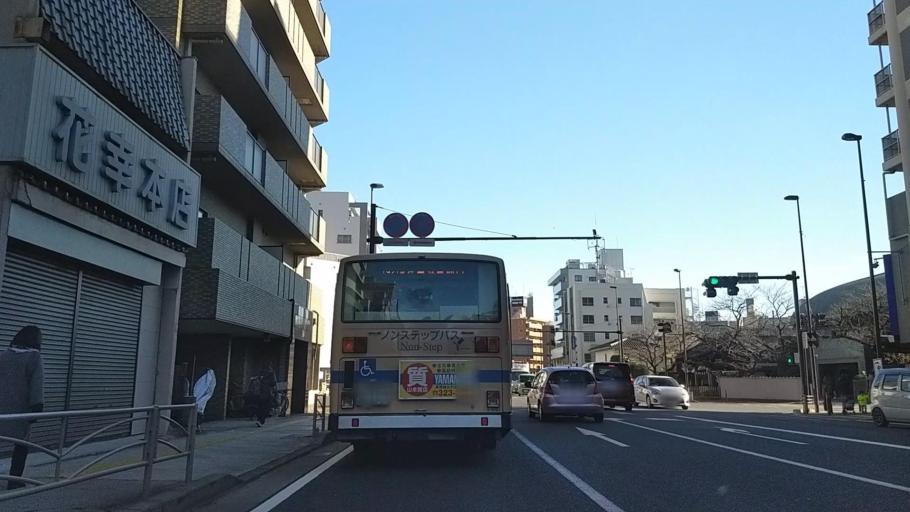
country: JP
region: Kanagawa
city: Yokohama
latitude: 35.4569
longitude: 139.6059
